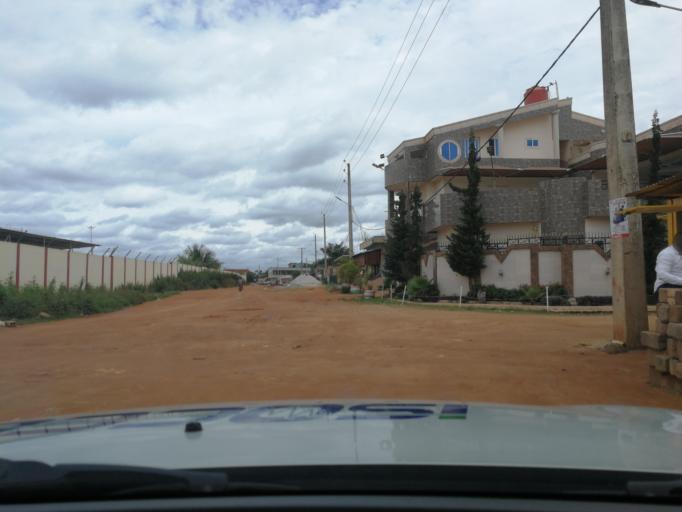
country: BJ
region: Atlantique
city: Abomey-Calavi
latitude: 6.4295
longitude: 2.3068
